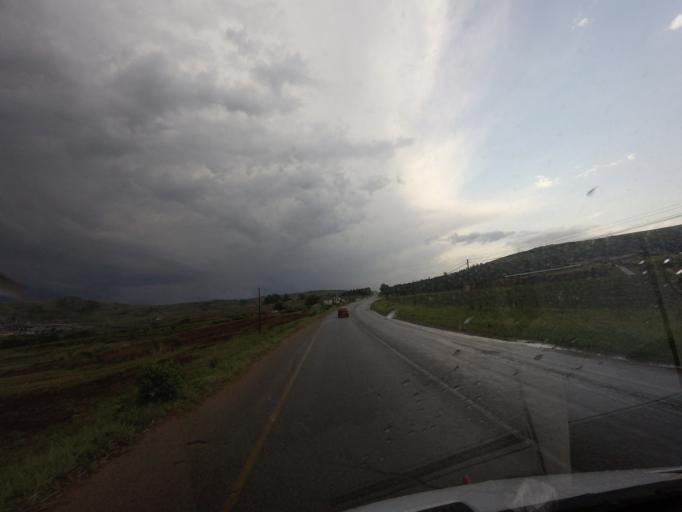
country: SZ
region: Manzini
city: Kwaluseni
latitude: -26.5118
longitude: 31.2642
